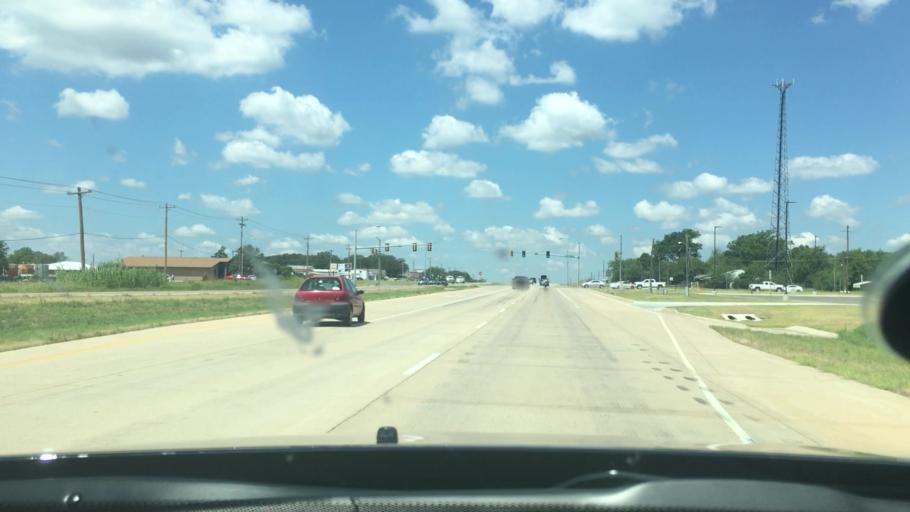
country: US
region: Oklahoma
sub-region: Carter County
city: Lone Grove
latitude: 34.1730
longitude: -97.2456
